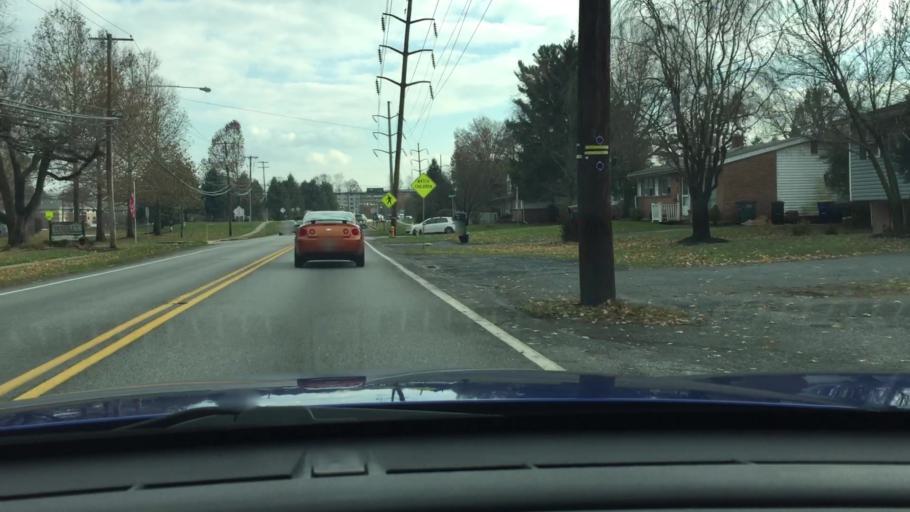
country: US
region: Pennsylvania
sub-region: Cumberland County
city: Shiremanstown
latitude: 40.2151
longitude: -76.9731
